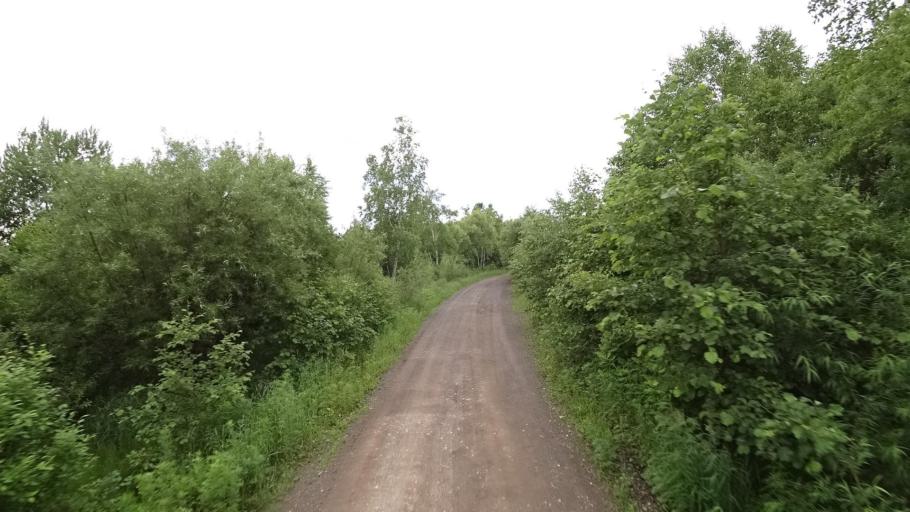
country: RU
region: Khabarovsk Krai
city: Amursk
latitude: 49.9116
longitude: 136.1581
